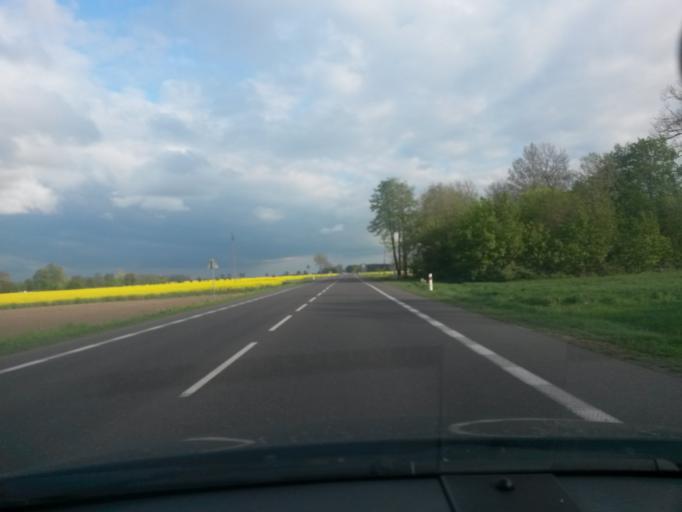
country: PL
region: Masovian Voivodeship
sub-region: Powiat plocki
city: Drobin
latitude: 52.7184
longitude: 20.0198
